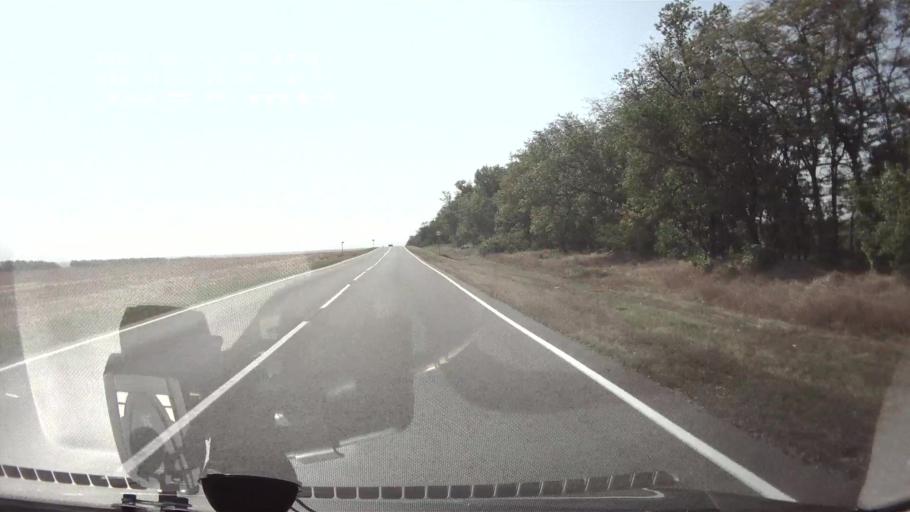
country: RU
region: Krasnodarskiy
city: Dmitriyevskaya
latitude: 45.7764
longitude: 40.7195
